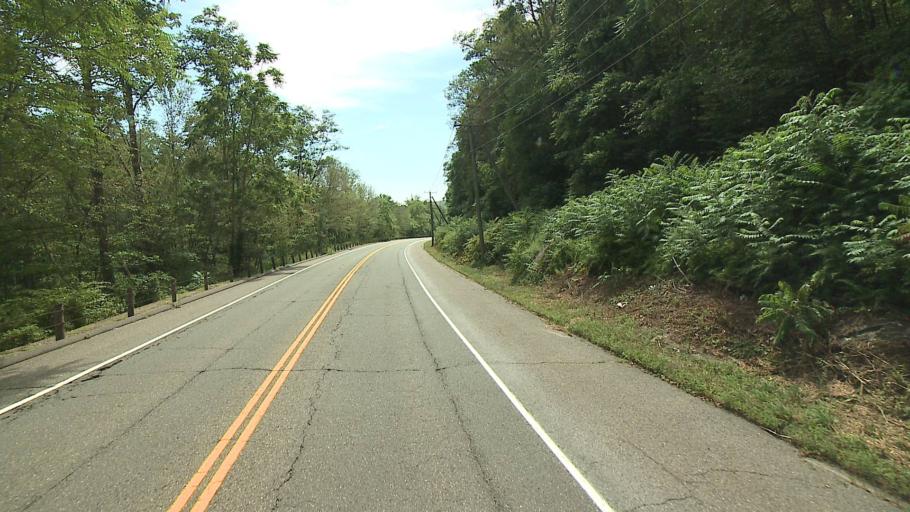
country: US
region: Connecticut
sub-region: Hartford County
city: Collinsville
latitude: 41.7977
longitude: -72.9263
